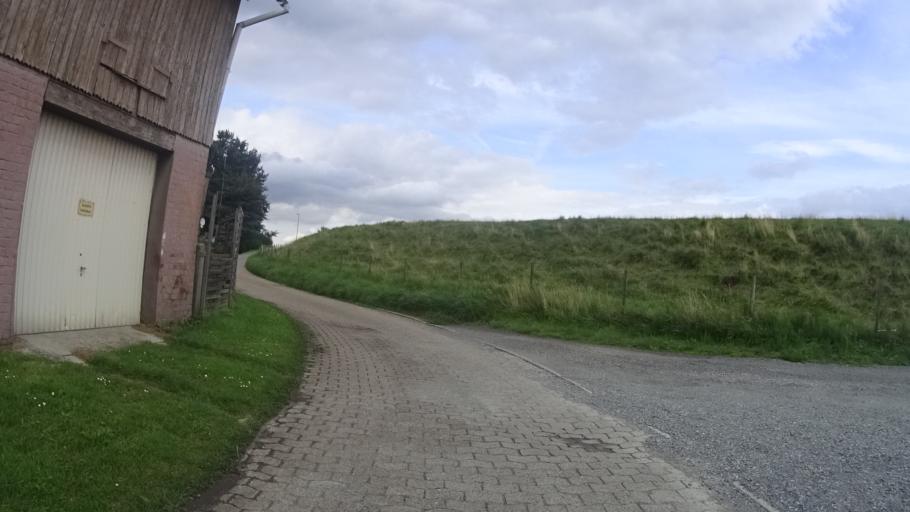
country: DE
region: Lower Saxony
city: Wischhafen
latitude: 53.7736
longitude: 9.3196
